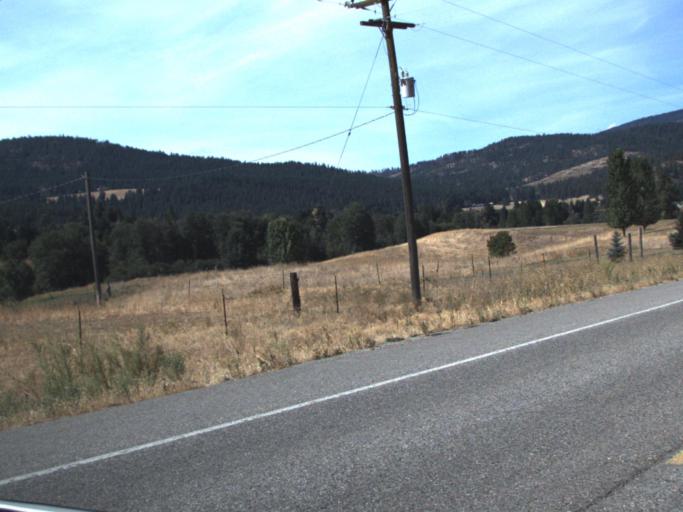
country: US
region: Washington
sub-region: Stevens County
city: Chewelah
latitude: 48.3147
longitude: -117.8070
